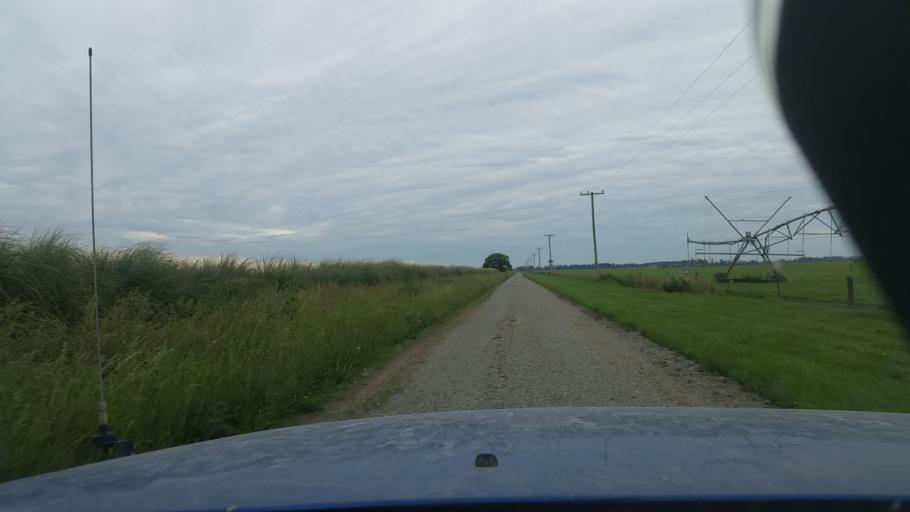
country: NZ
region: Canterbury
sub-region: Ashburton District
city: Tinwald
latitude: -43.9384
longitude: 171.5631
